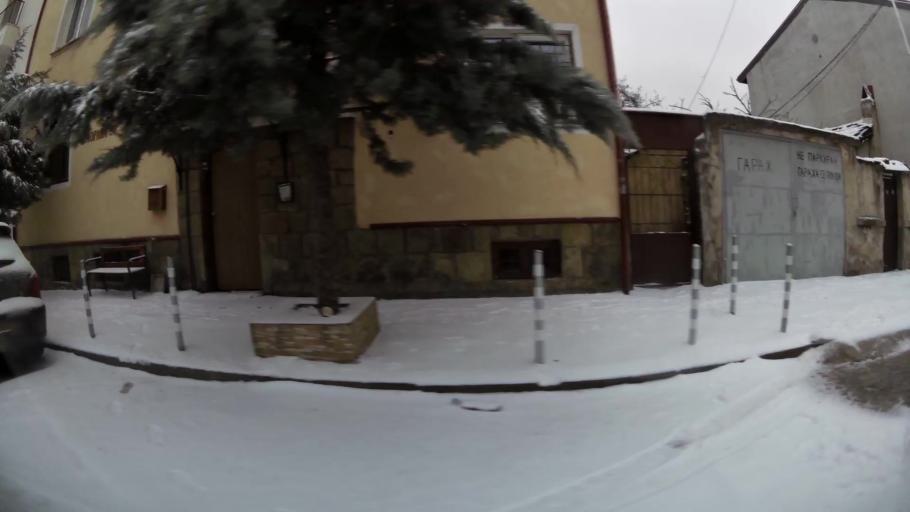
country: BG
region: Sofia-Capital
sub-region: Stolichna Obshtina
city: Sofia
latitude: 42.7034
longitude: 23.3072
